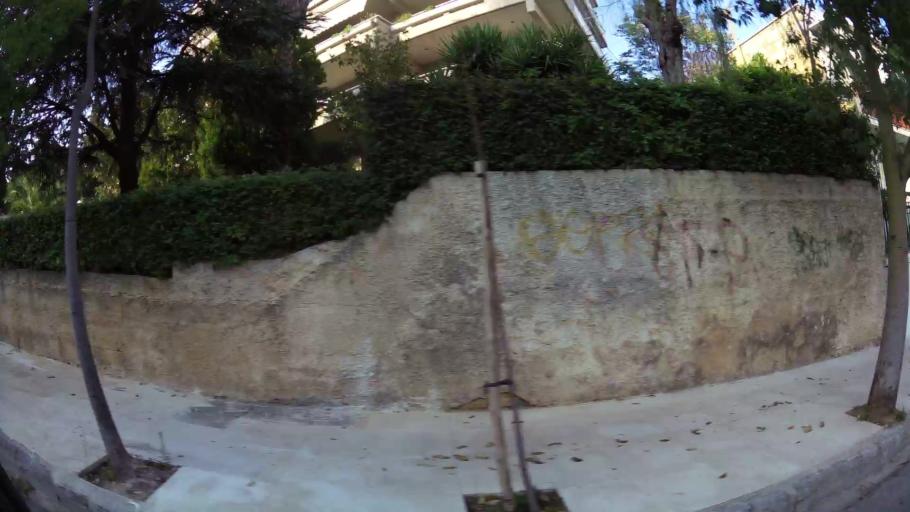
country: GR
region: Attica
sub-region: Nomarchia Athinas
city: Irakleio
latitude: 38.0477
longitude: 23.7736
